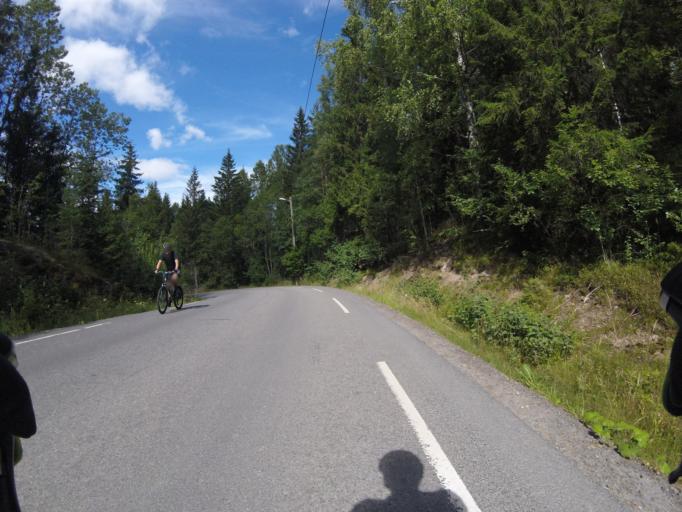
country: NO
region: Akershus
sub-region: Lorenskog
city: Kjenn
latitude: 59.8952
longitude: 10.9746
